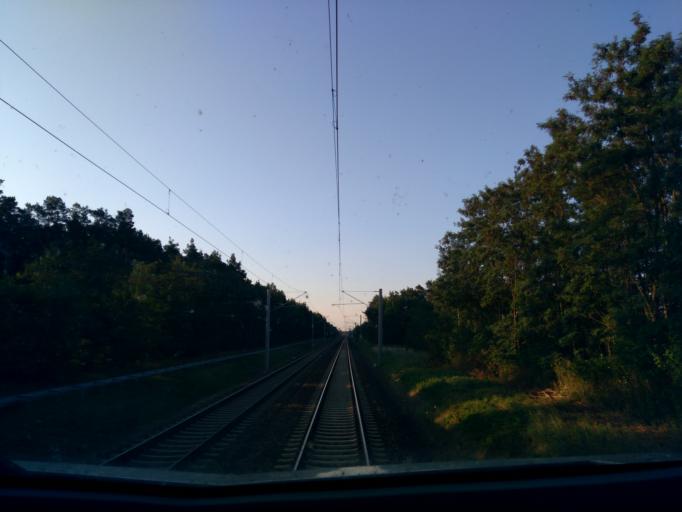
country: DE
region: Brandenburg
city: Halbe
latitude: 52.1236
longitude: 13.6857
